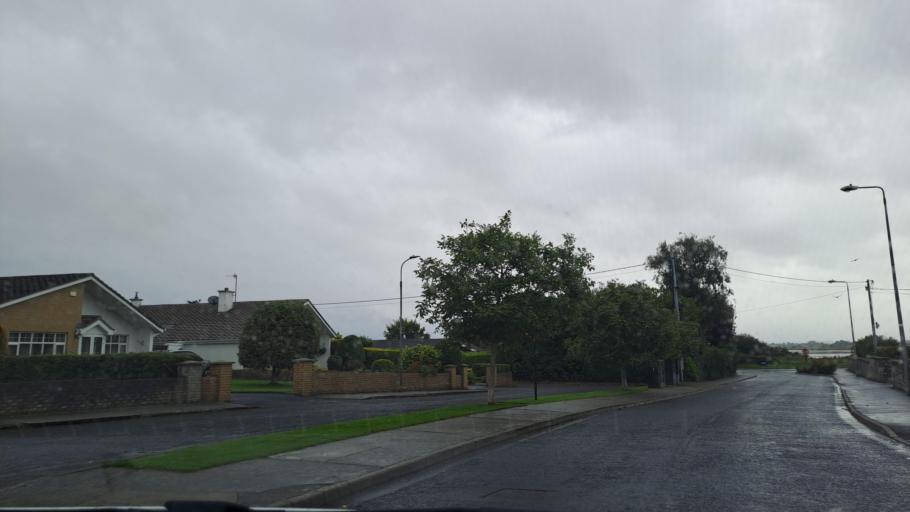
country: IE
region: Leinster
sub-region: Lu
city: Blackrock
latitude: 53.9583
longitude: -6.3753
